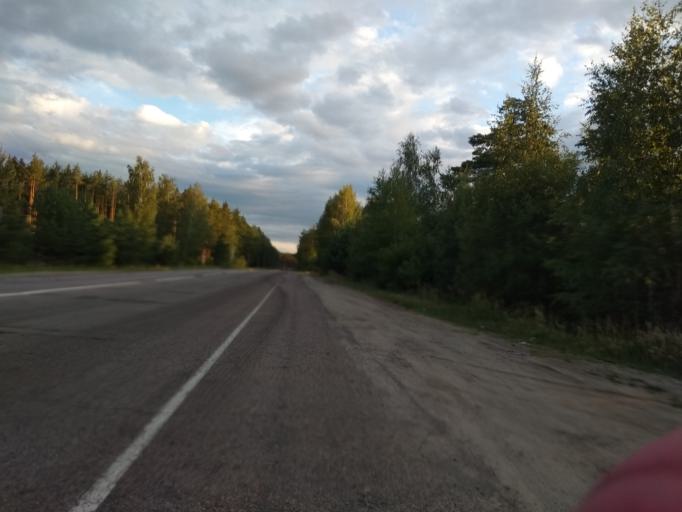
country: RU
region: Moskovskaya
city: Misheronskiy
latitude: 55.6334
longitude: 39.7456
